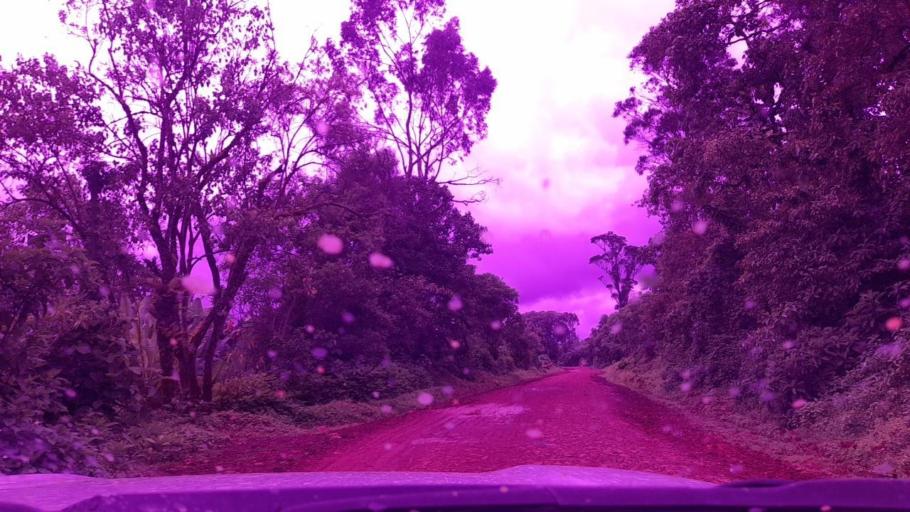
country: ET
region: Southern Nations, Nationalities, and People's Region
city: Tippi
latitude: 7.5690
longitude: 35.6502
